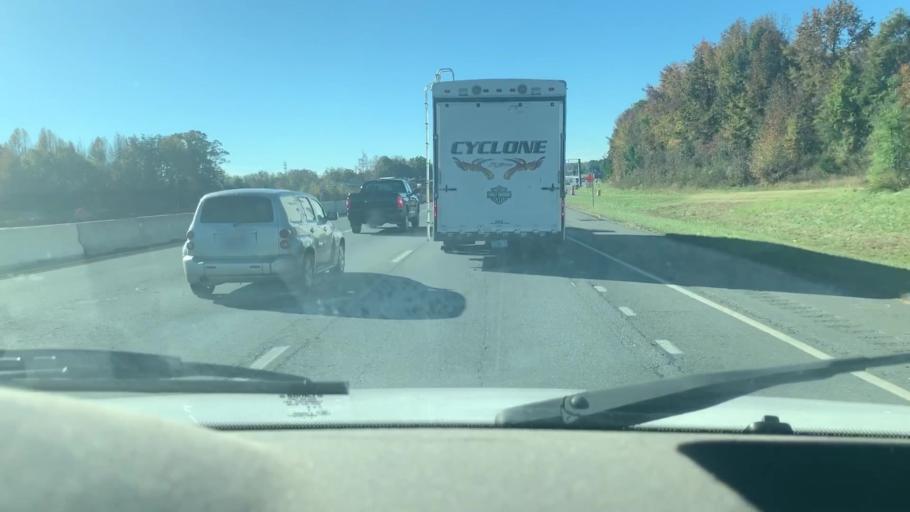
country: US
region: North Carolina
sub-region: Mecklenburg County
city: Huntersville
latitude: 35.3608
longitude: -80.8430
